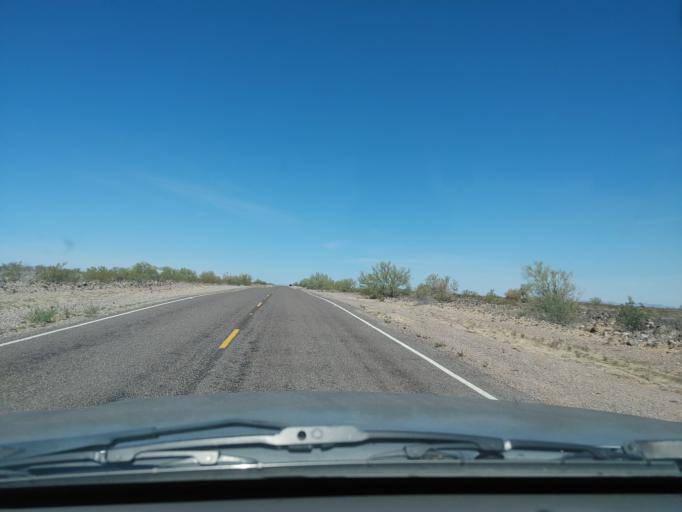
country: US
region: Arizona
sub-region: Maricopa County
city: Gila Bend
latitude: 32.8824
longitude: -113.2289
